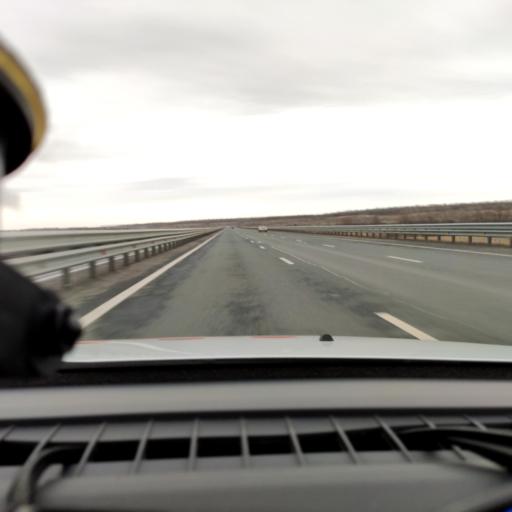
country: RU
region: Samara
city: Smyshlyayevka
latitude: 53.1558
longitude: 50.3418
